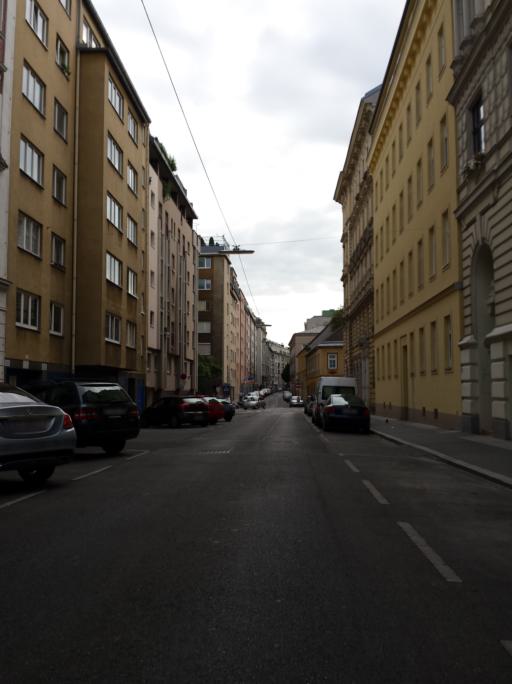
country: AT
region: Vienna
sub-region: Wien Stadt
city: Vienna
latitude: 48.1939
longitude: 16.3478
